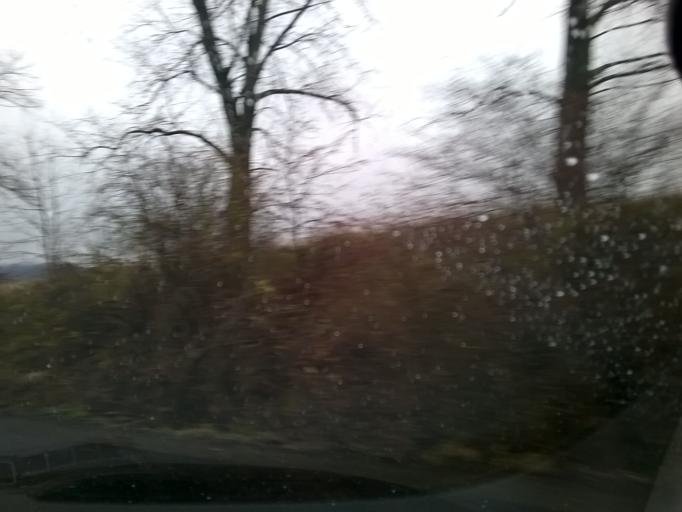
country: SK
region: Nitriansky
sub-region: Okres Nitra
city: Nitra
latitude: 48.3378
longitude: 18.0263
